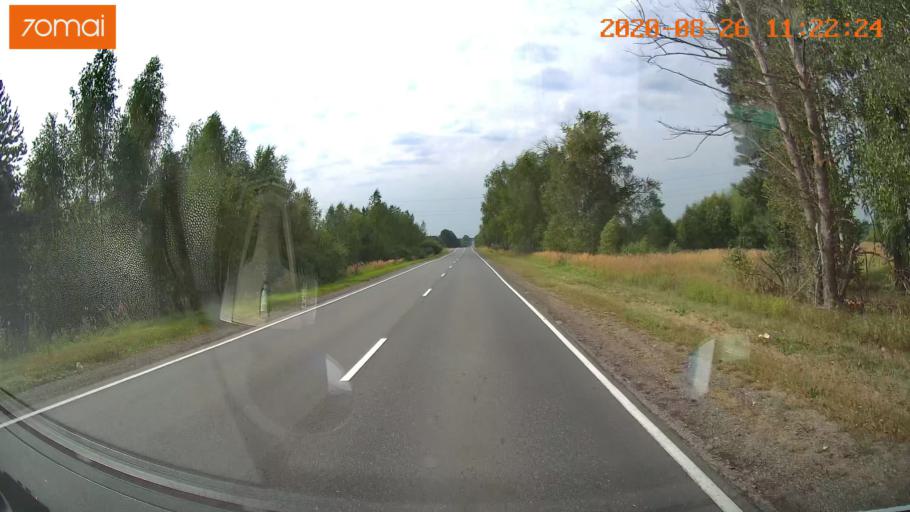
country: RU
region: Rjazan
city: Shilovo
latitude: 54.3645
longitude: 41.0279
